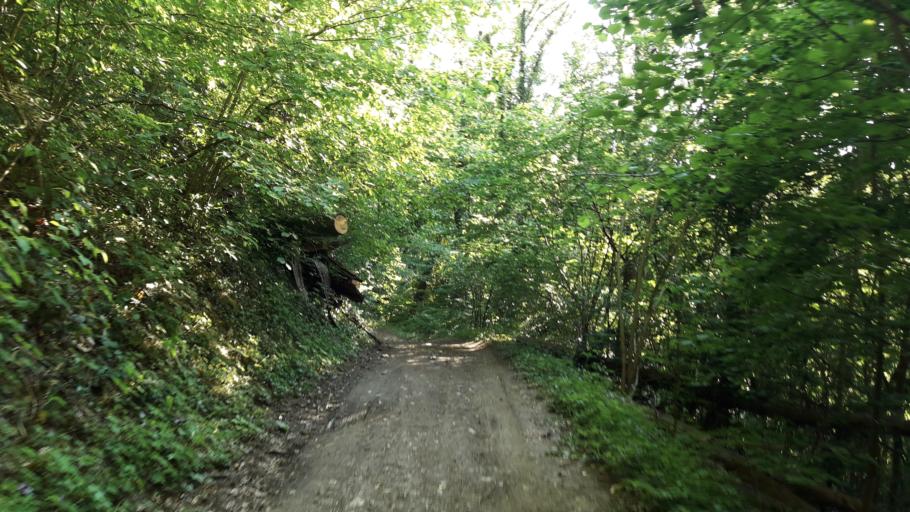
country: FR
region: Rhone-Alpes
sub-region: Departement de l'Isere
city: Poisat
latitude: 45.1577
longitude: 5.7773
